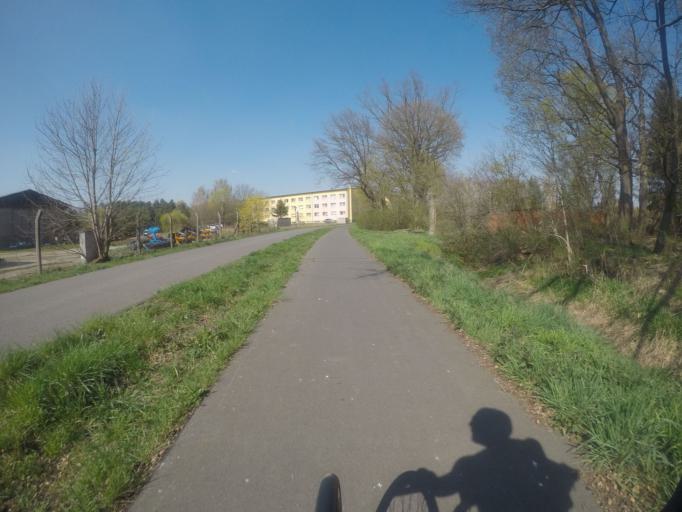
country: DE
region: Brandenburg
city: Falkensee
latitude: 52.6372
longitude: 13.0844
